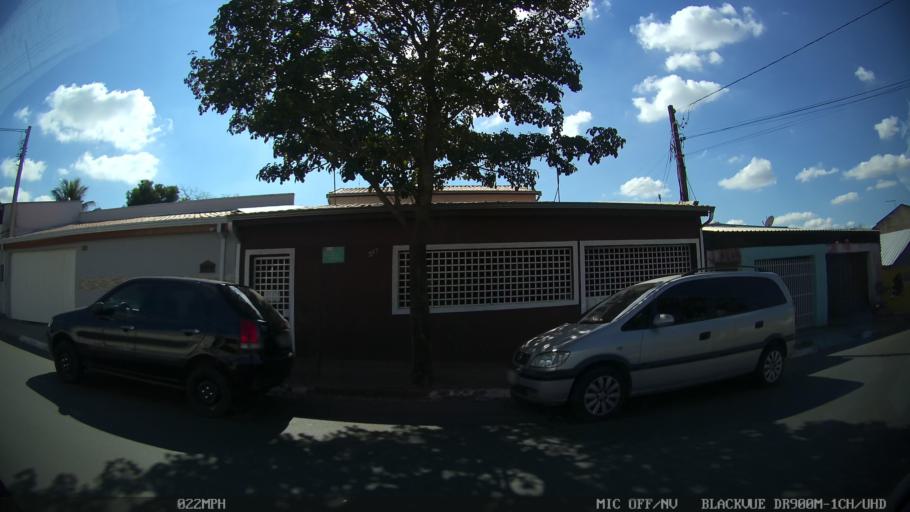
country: BR
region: Sao Paulo
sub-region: Hortolandia
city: Hortolandia
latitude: -22.8914
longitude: -47.2184
